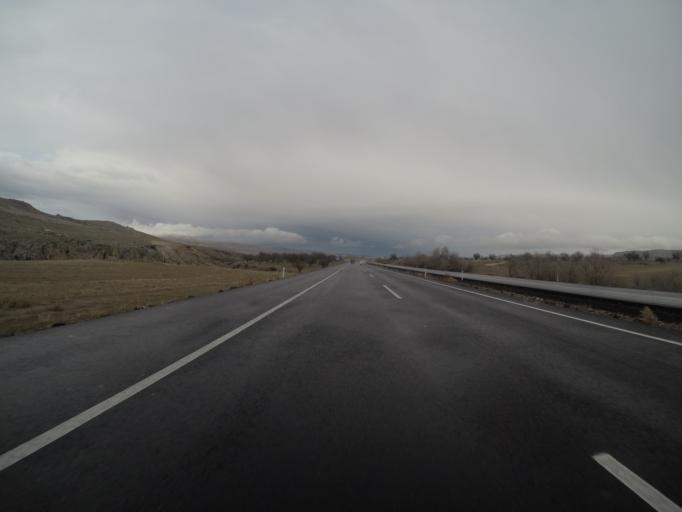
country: TR
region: Nevsehir
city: Avanos
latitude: 38.6852
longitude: 34.8049
